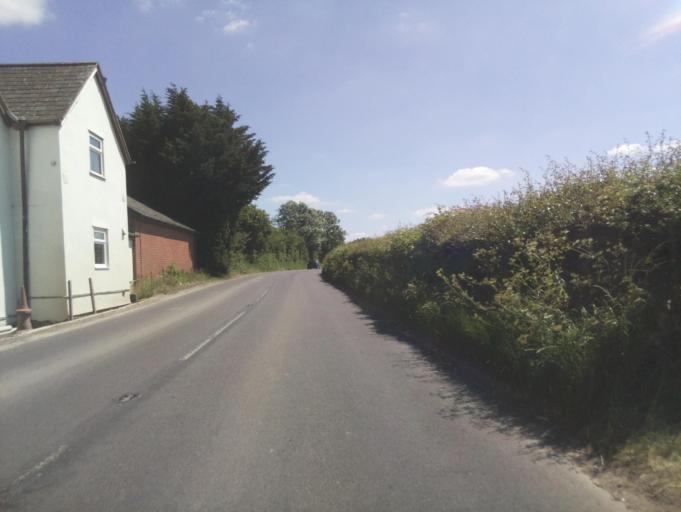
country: GB
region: England
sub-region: Wiltshire
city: Royal Wootton Bassett
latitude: 51.5268
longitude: -1.8925
